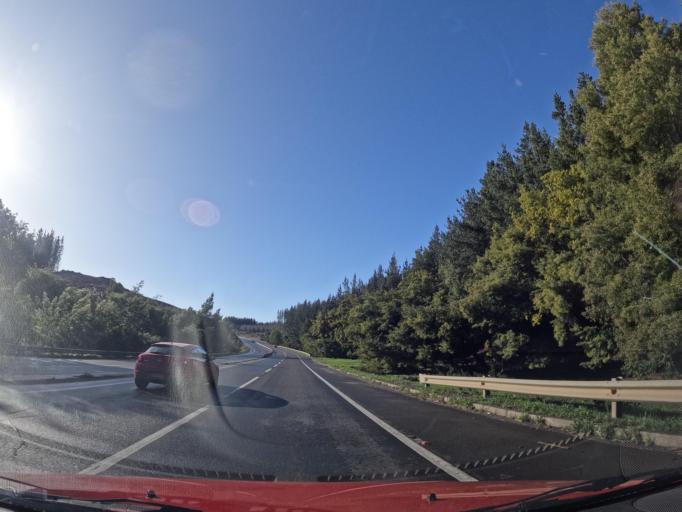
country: CL
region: Biobio
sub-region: Provincia de Concepcion
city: Penco
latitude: -36.7591
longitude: -72.9439
